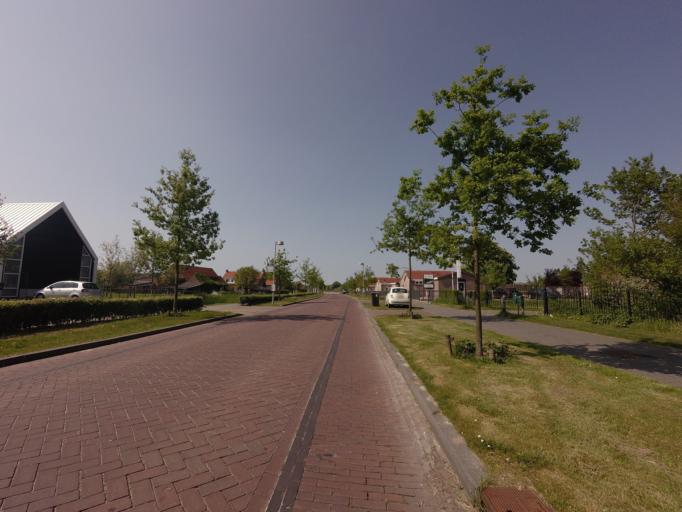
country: NL
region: Zeeland
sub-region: Gemeente Middelburg
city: Middelburg
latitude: 51.5535
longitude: 3.5875
